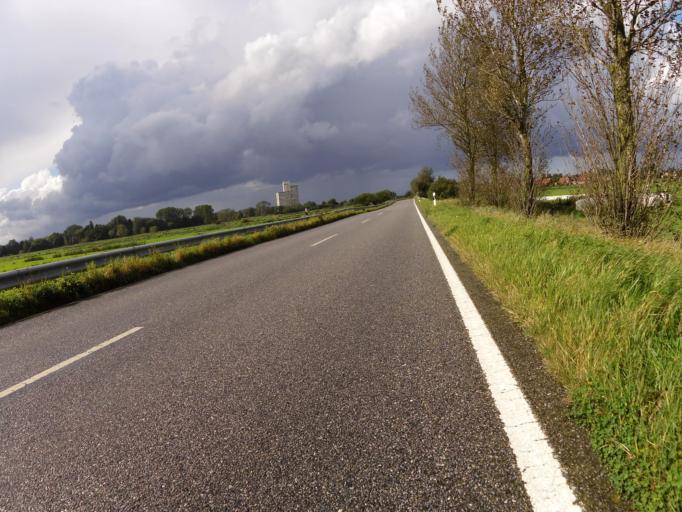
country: DE
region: Schleswig-Holstein
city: Wisch
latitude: 54.4218
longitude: 10.3851
